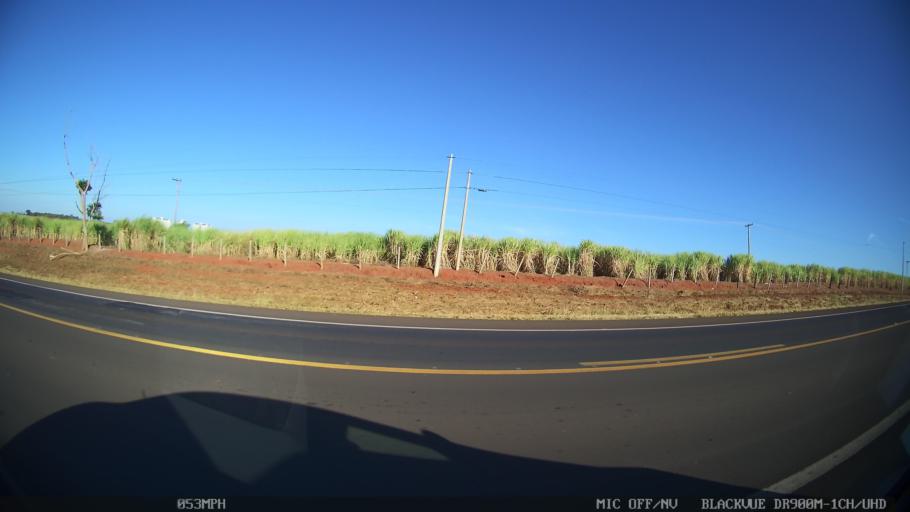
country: BR
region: Sao Paulo
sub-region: Olimpia
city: Olimpia
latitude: -20.6973
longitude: -48.9318
